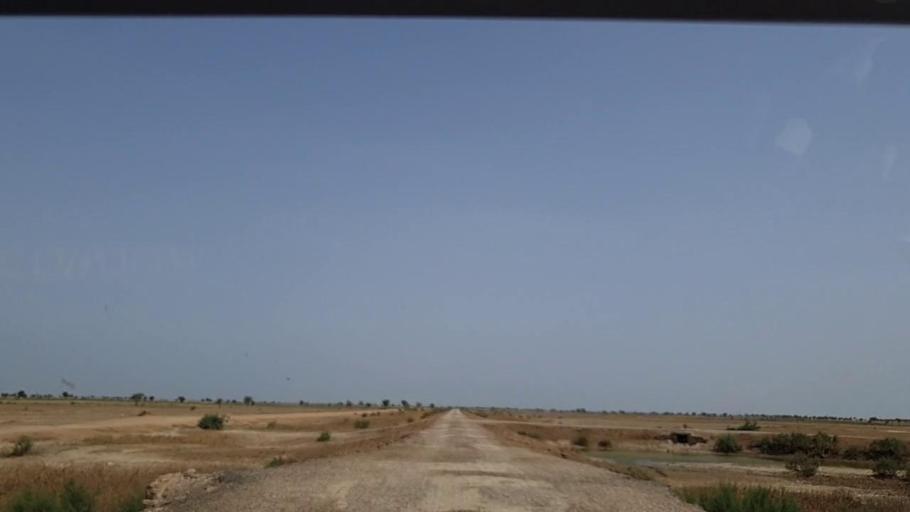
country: PK
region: Sindh
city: Johi
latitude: 26.7830
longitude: 67.6481
